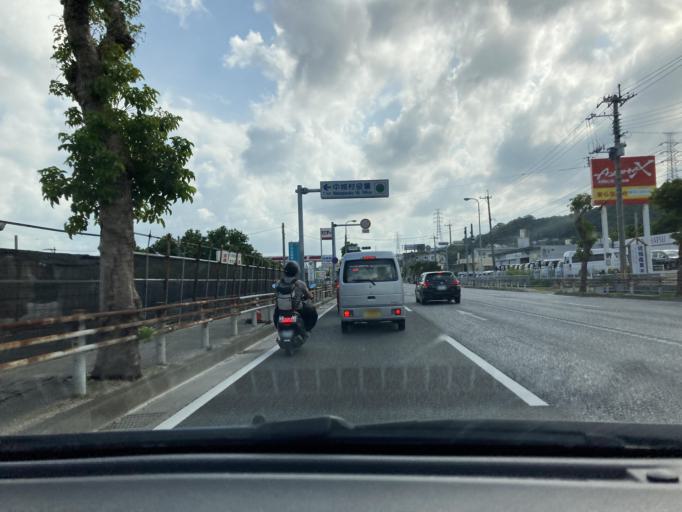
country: JP
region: Okinawa
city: Ginowan
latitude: 26.2634
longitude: 127.7891
